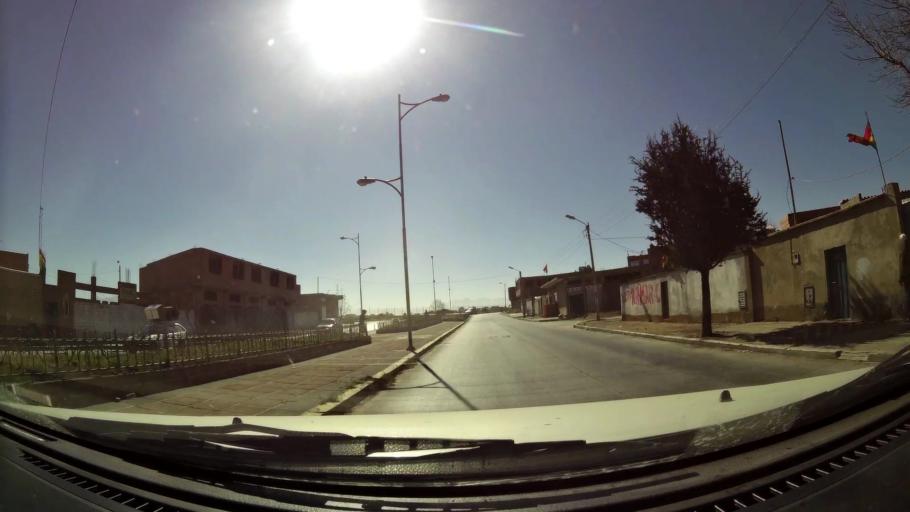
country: BO
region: La Paz
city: La Paz
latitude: -16.5166
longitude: -68.1809
